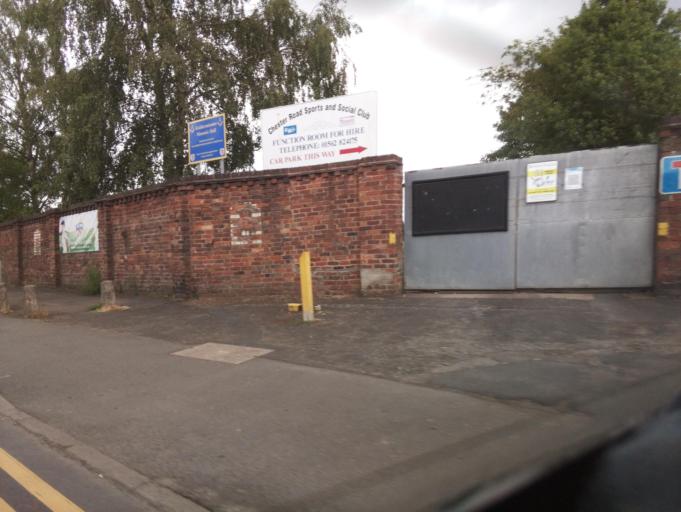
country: GB
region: England
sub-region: Worcestershire
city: Kidderminster
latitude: 52.3883
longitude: -2.2333
